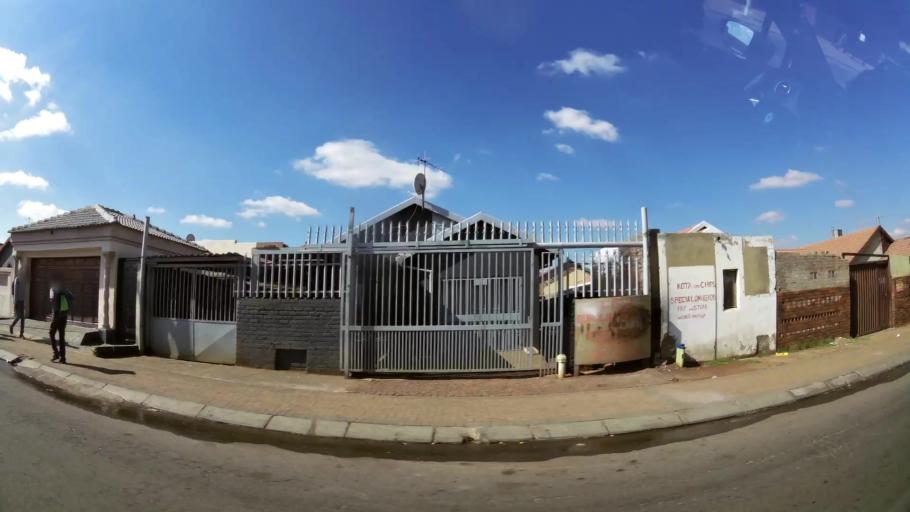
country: ZA
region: Gauteng
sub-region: West Rand District Municipality
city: Krugersdorp
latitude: -26.1627
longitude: 27.7806
